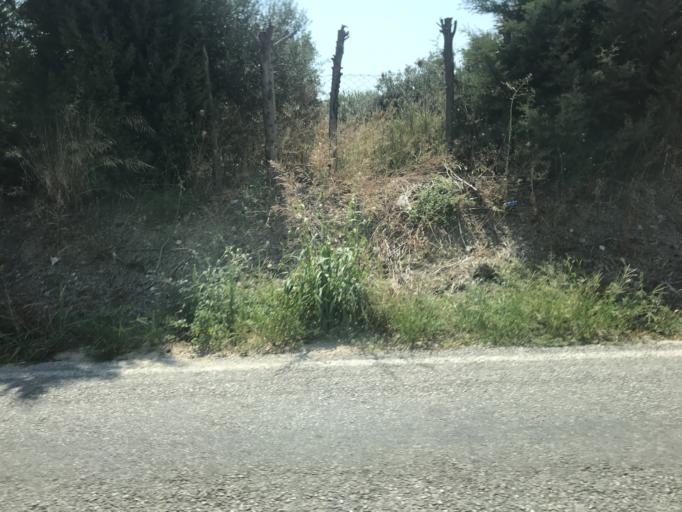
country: TR
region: Izmir
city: Urla
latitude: 38.3134
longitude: 26.7614
